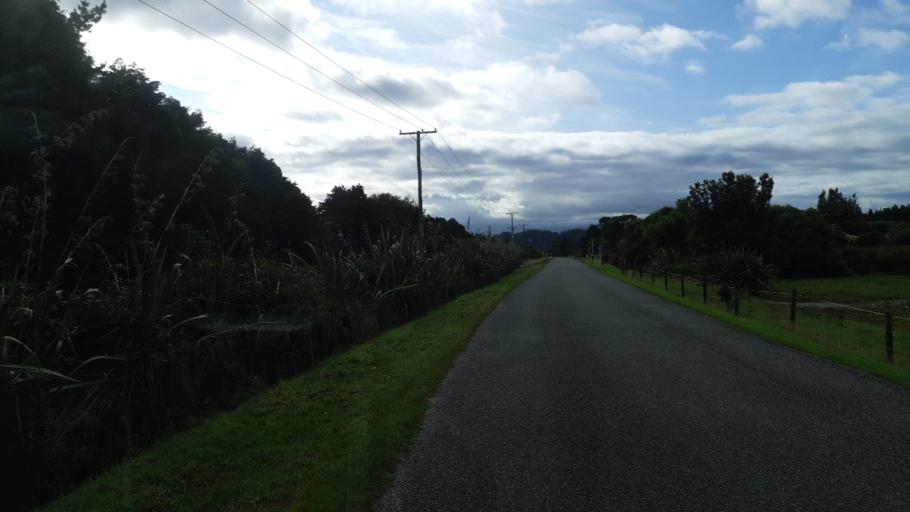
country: NZ
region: West Coast
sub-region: Westland District
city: Hokitika
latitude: -42.7299
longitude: 170.9596
